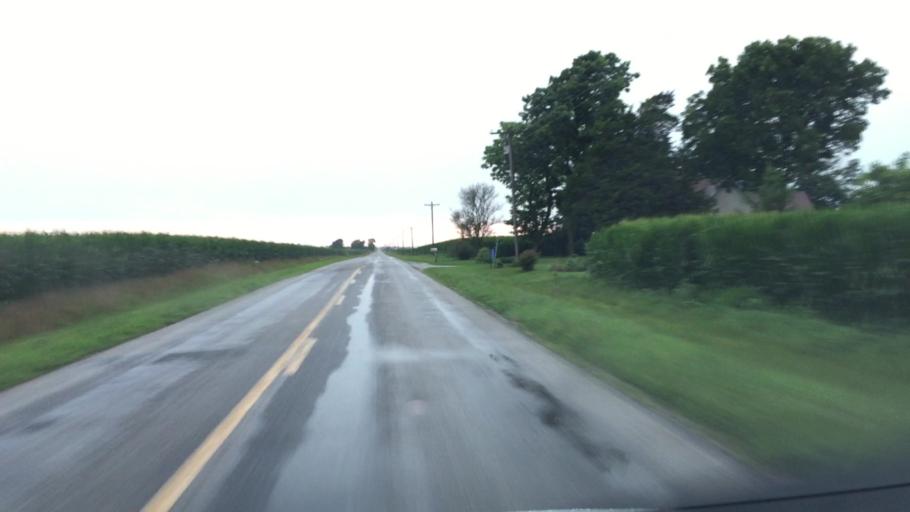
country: US
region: Iowa
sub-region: Lee County
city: Fort Madison
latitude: 40.5209
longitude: -91.2533
